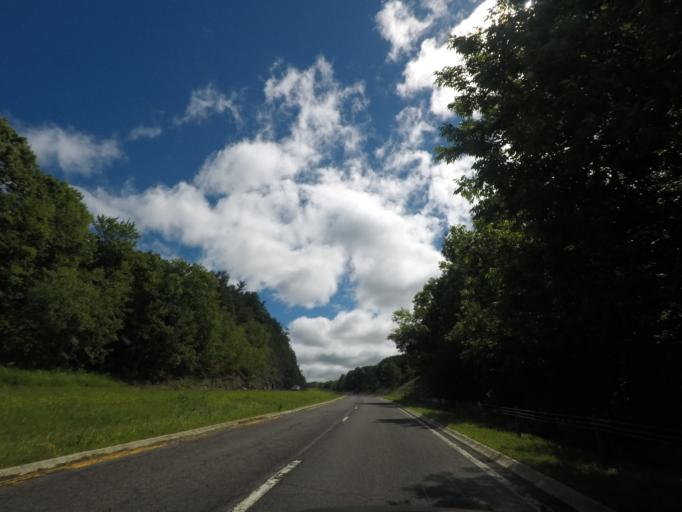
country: US
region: New York
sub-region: Columbia County
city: Chatham
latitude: 42.3256
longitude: -73.5736
